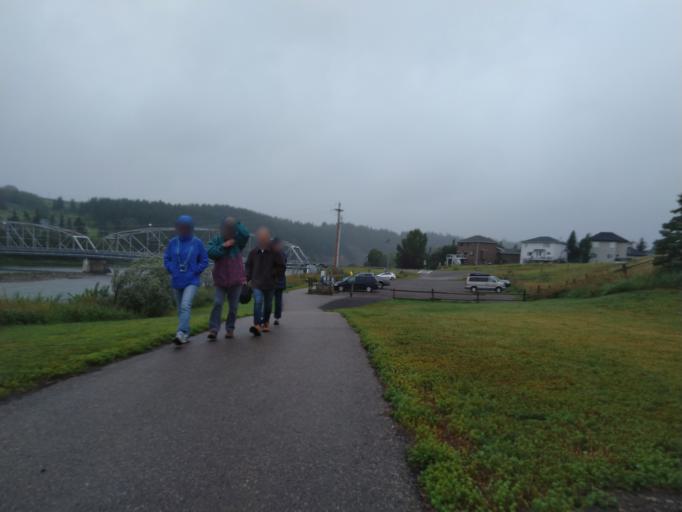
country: CA
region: Alberta
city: Cochrane
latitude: 51.1740
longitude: -114.4651
